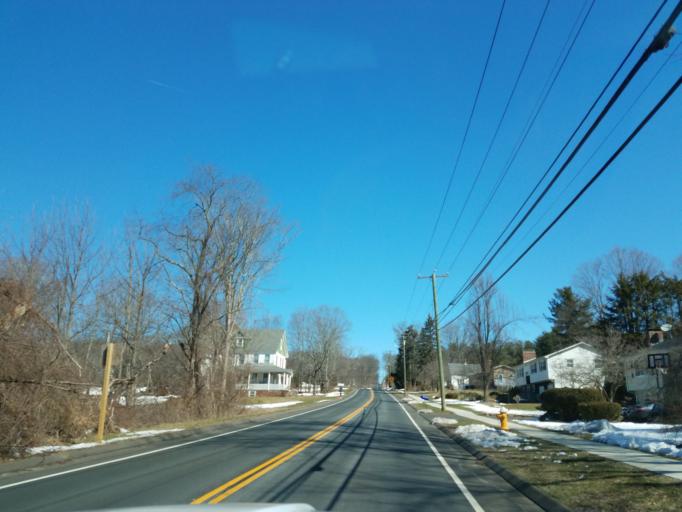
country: US
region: Connecticut
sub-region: Hartford County
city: Manchester
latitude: 41.8295
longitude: -72.5168
